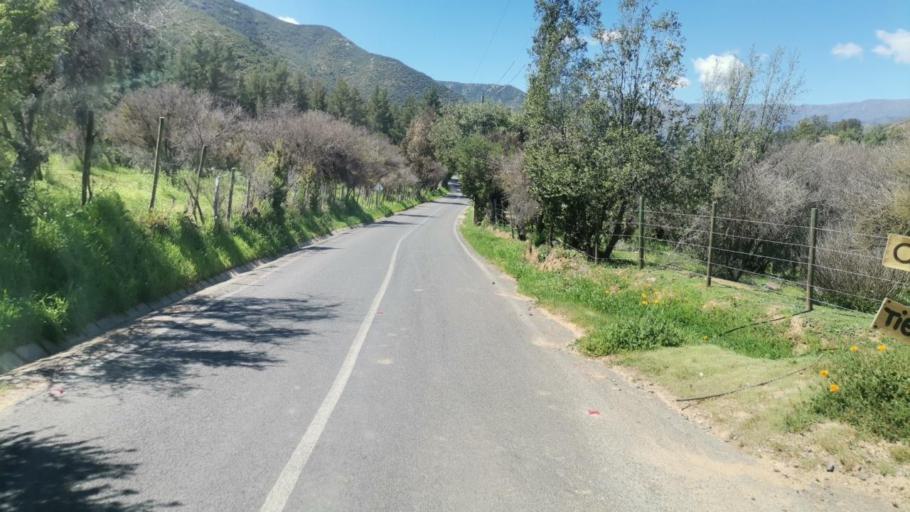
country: CL
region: Valparaiso
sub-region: Provincia de Marga Marga
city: Limache
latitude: -33.1700
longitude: -71.1587
